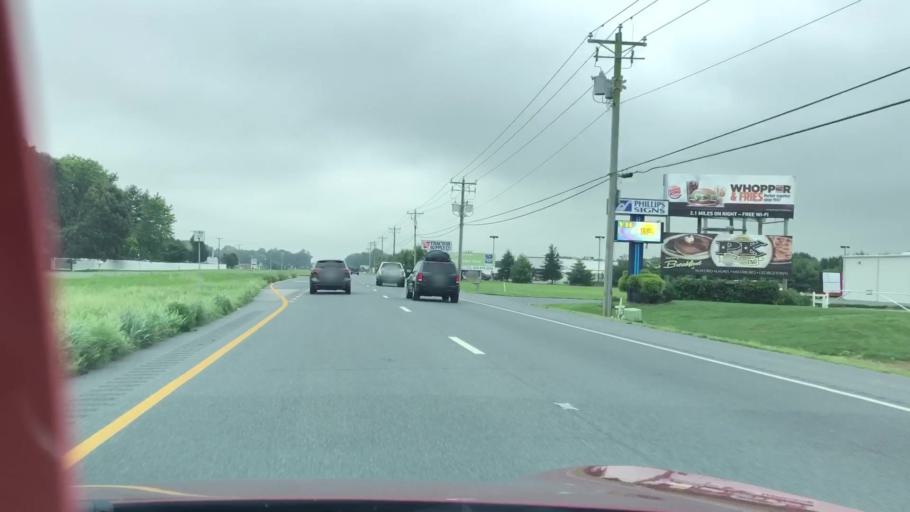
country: US
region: Delaware
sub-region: Sussex County
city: Bridgeville
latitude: 38.6908
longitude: -75.5904
